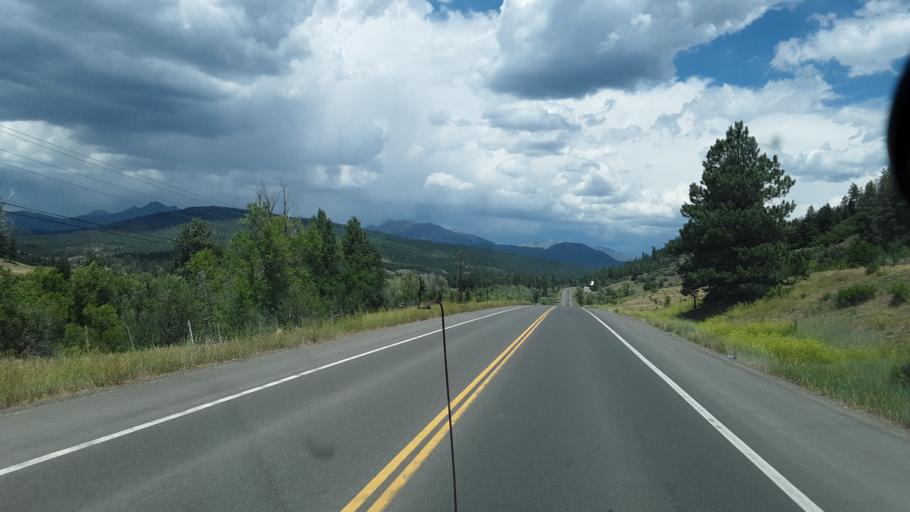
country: US
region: Colorado
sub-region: Archuleta County
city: Pagosa Springs
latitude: 37.2967
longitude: -106.9723
